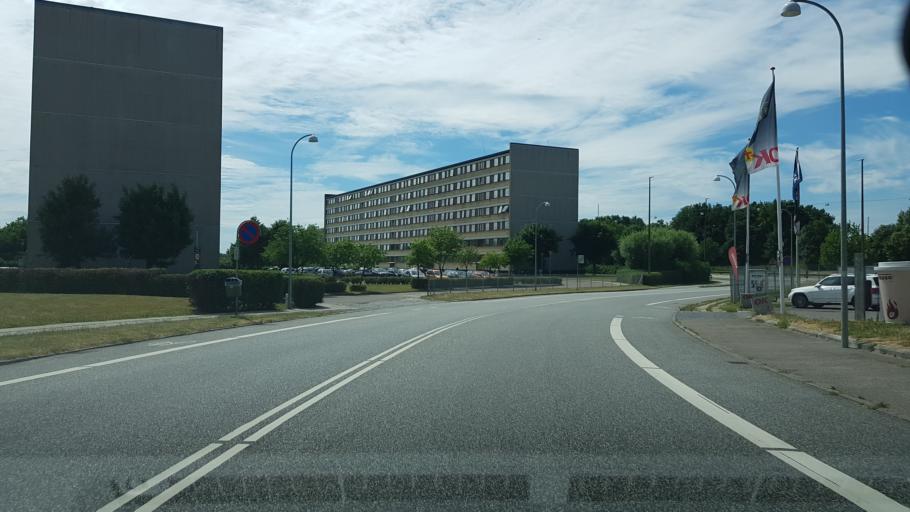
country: DK
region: Capital Region
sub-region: Rodovre Kommune
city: Rodovre
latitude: 55.6633
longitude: 12.4569
